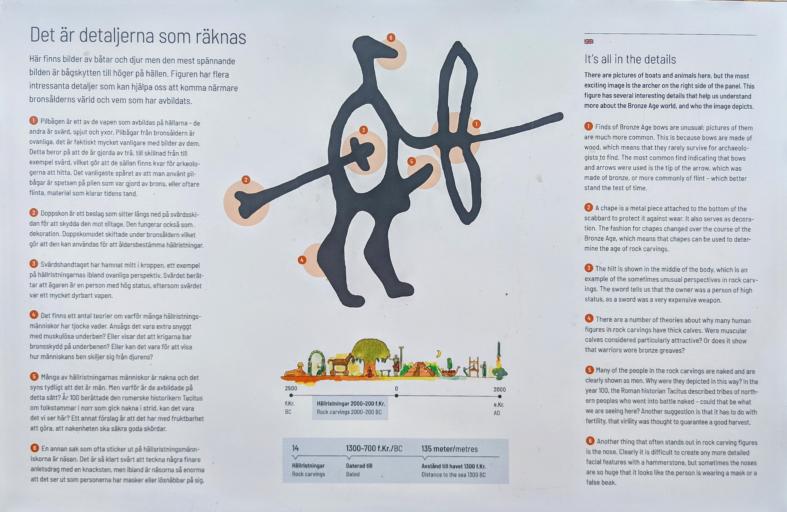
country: SE
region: Vaestra Goetaland
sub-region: Tanums Kommun
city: Tanumshede
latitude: 58.6997
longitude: 11.3365
